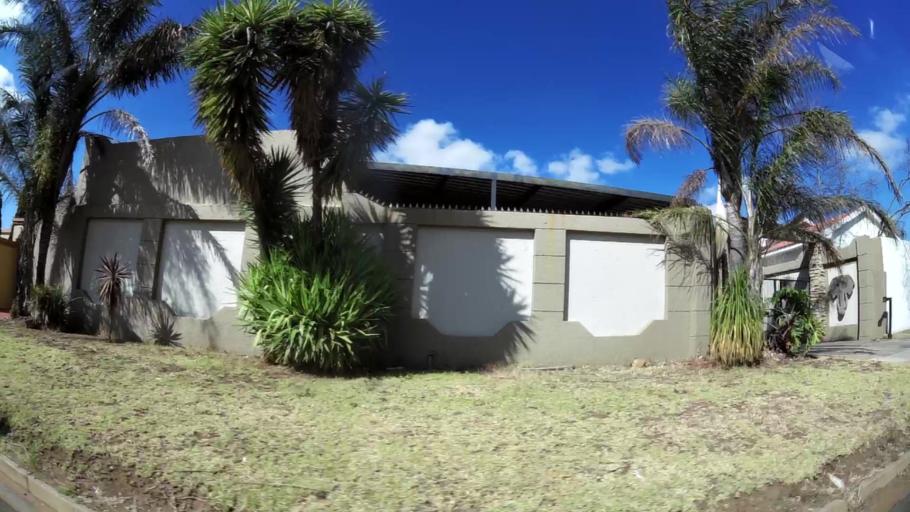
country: ZA
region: Gauteng
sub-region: West Rand District Municipality
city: Krugersdorp
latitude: -26.0915
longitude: 27.7859
